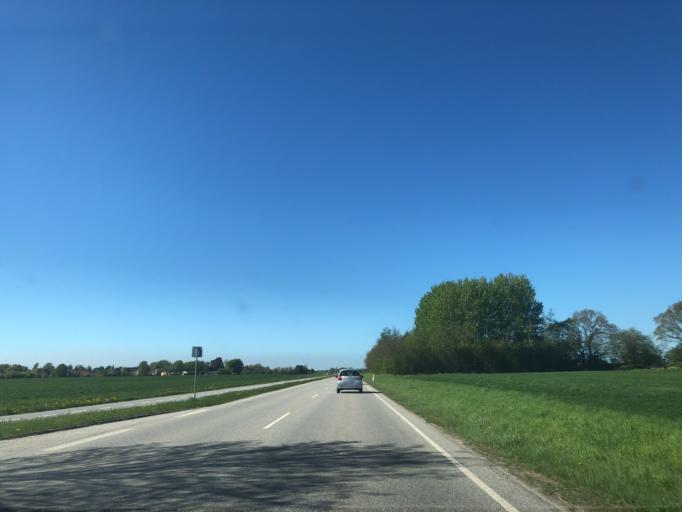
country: DK
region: Zealand
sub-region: Stevns Kommune
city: Store Heddinge
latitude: 55.3447
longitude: 12.3378
